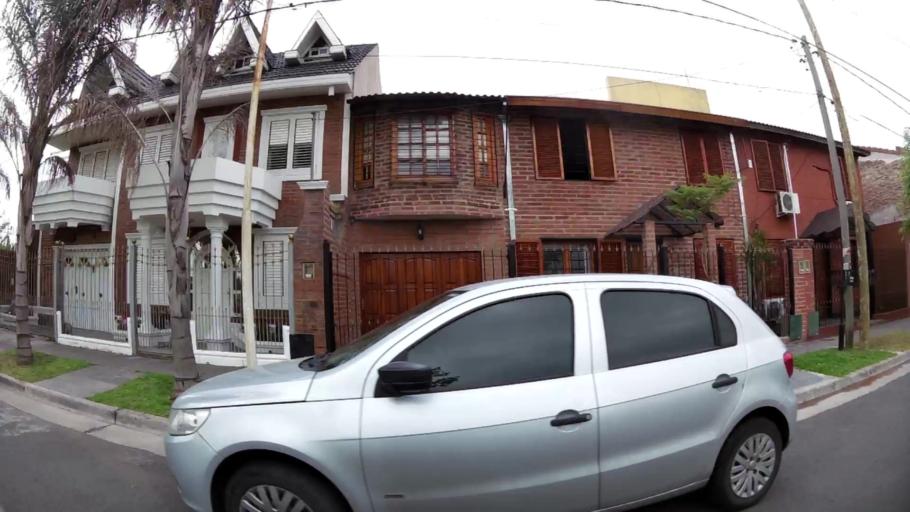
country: AR
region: Buenos Aires
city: San Justo
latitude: -34.7134
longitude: -58.5269
